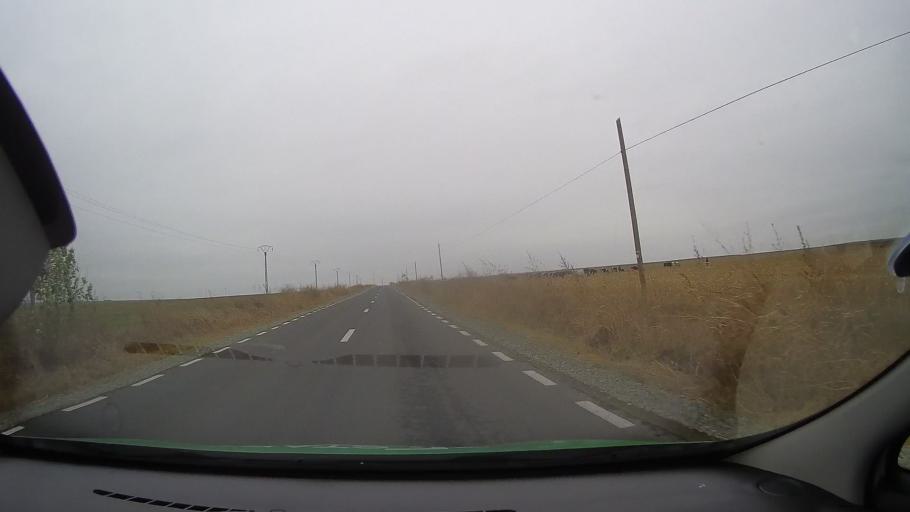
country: RO
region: Constanta
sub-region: Comuna Tortoman
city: Tortoman
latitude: 44.3537
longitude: 28.2143
